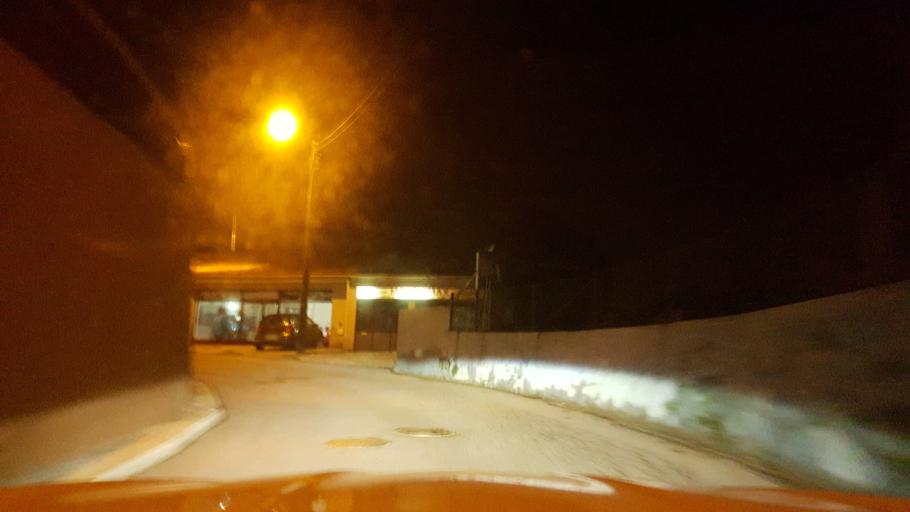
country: PT
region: Porto
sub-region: Matosinhos
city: Guifoes
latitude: 41.2133
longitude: -8.6510
